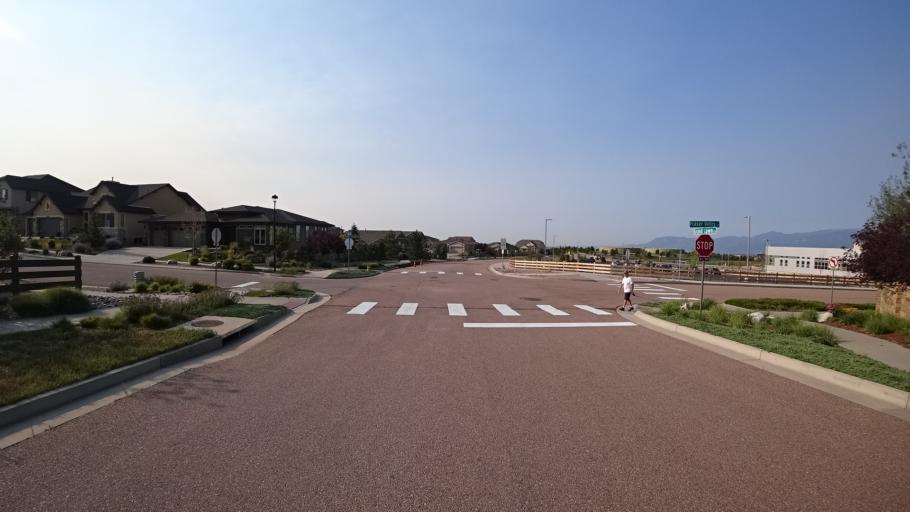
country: US
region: Colorado
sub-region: El Paso County
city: Black Forest
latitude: 38.9754
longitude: -104.7315
